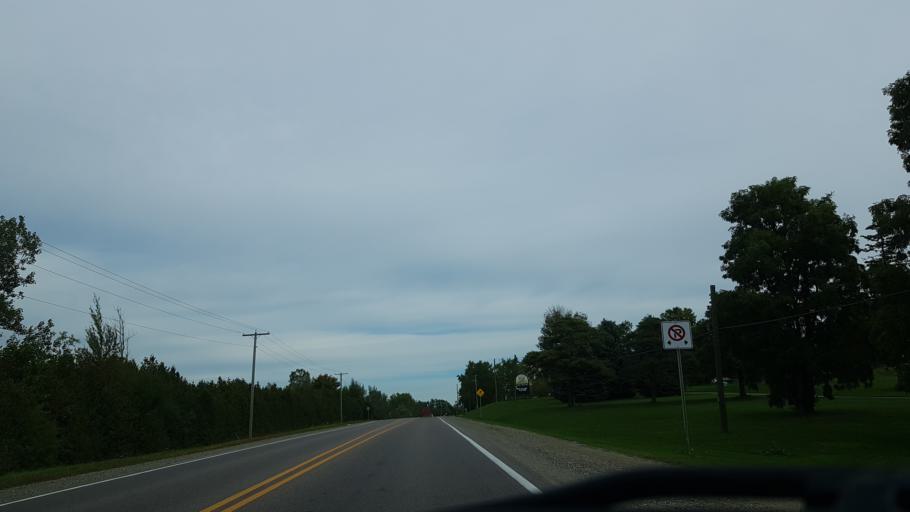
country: CA
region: Ontario
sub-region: Wellington County
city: Guelph
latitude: 43.6004
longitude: -80.2325
